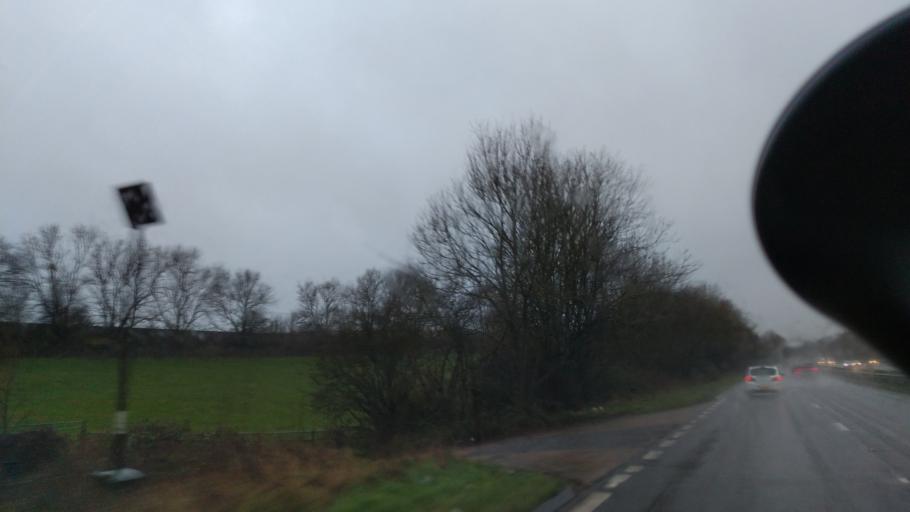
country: GB
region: England
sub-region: Brighton and Hove
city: Rottingdean
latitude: 50.8653
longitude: -0.0487
